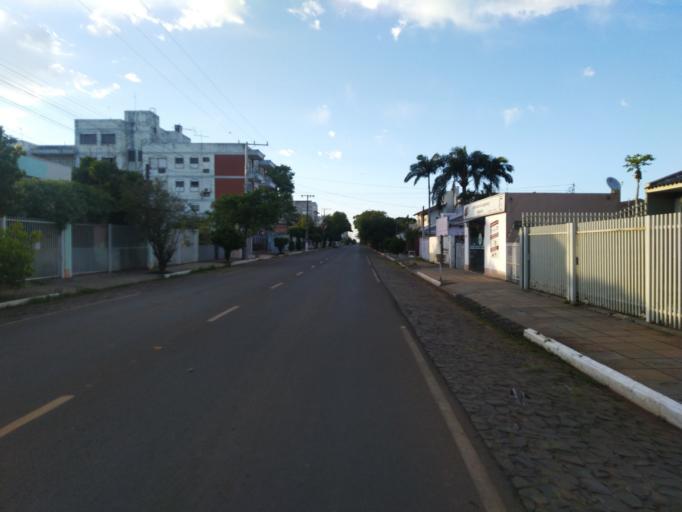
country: BR
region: Rio Grande do Sul
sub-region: Sao Borja
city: Sao Borja
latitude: -28.6584
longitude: -56.0094
